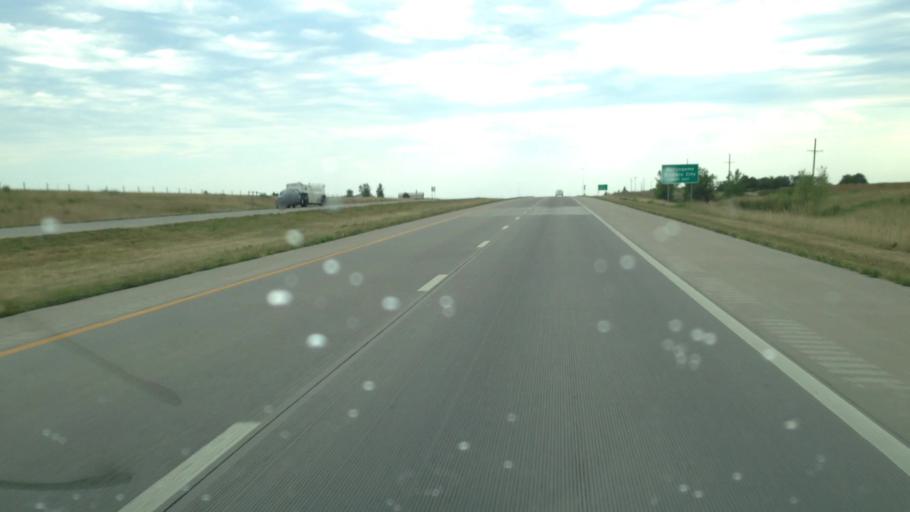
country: US
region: Kansas
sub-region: Douglas County
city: Baldwin City
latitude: 38.7943
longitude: -95.2690
